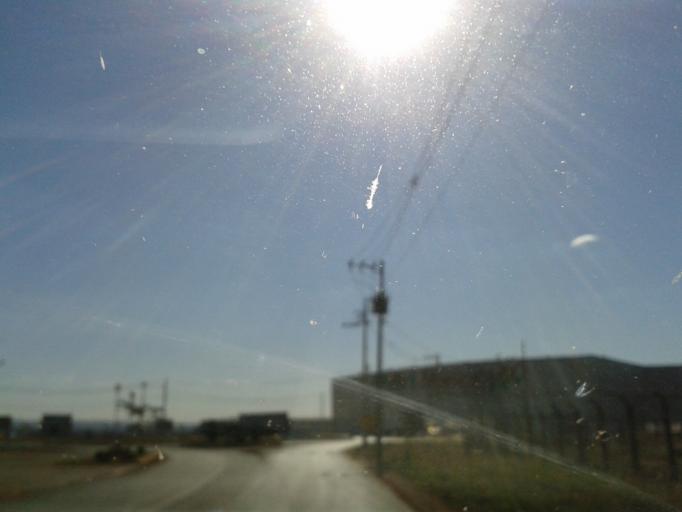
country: BR
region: Goias
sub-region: Itumbiara
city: Itumbiara
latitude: -18.4287
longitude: -49.1937
